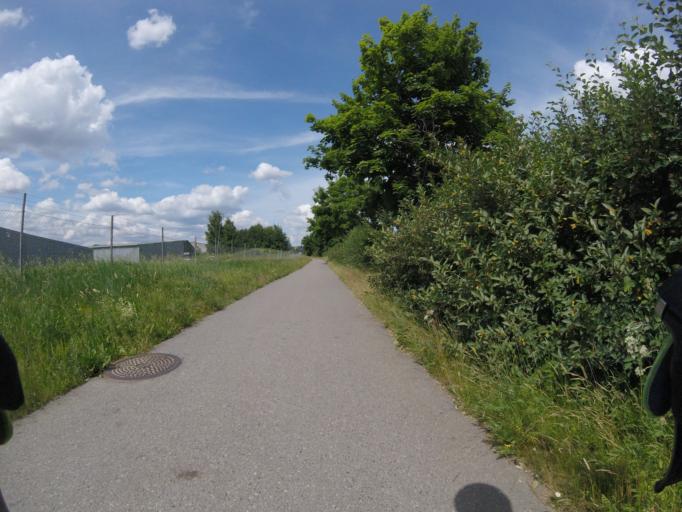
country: NO
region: Akershus
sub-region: Skedsmo
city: Lillestrom
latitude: 59.9686
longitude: 11.0509
